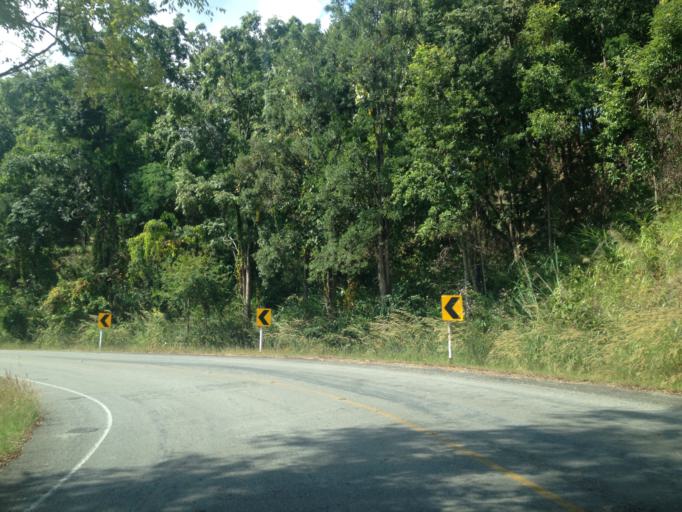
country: TH
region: Chiang Mai
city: Samoeng
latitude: 18.8057
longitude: 98.8103
